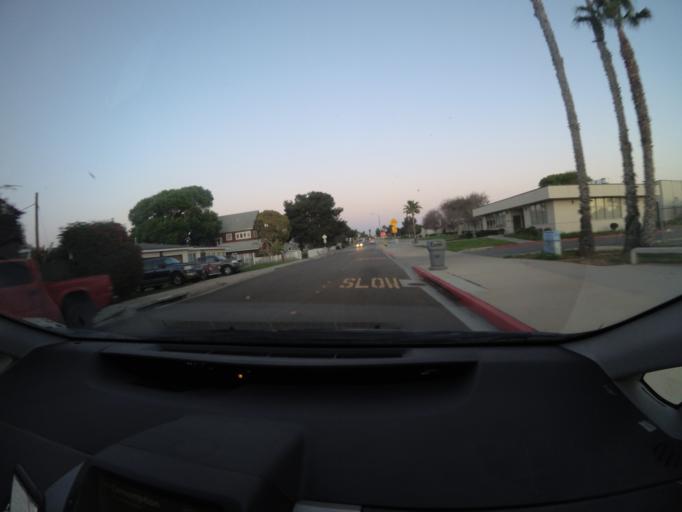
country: US
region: California
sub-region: San Diego County
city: Imperial Beach
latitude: 32.5803
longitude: -117.1234
